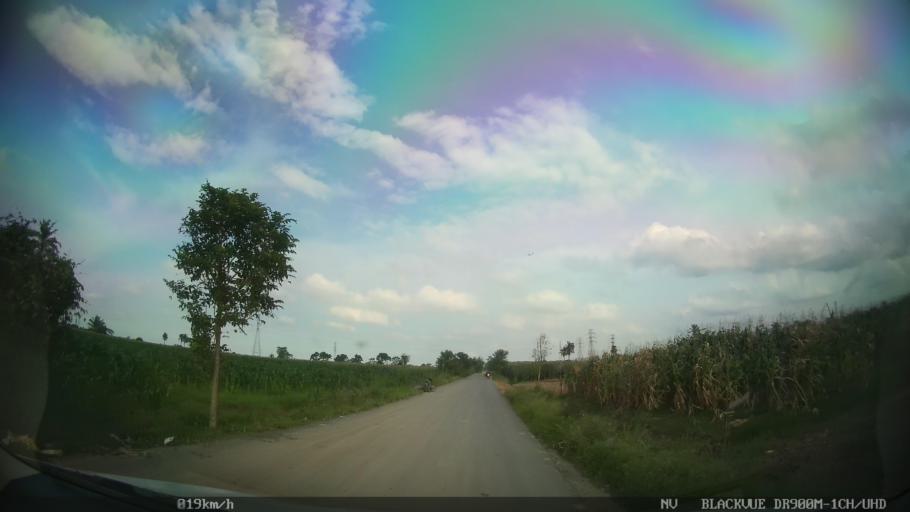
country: ID
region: North Sumatra
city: Percut
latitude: 3.5694
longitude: 98.7793
